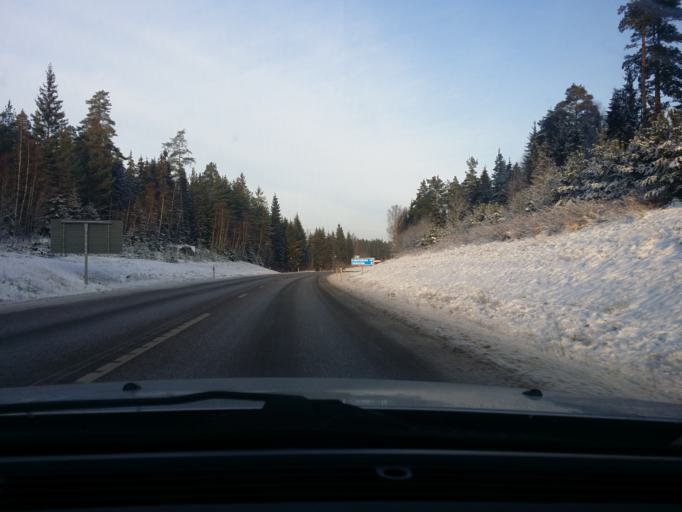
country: SE
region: OErebro
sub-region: Lindesbergs Kommun
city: Frovi
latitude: 59.4817
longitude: 15.3787
